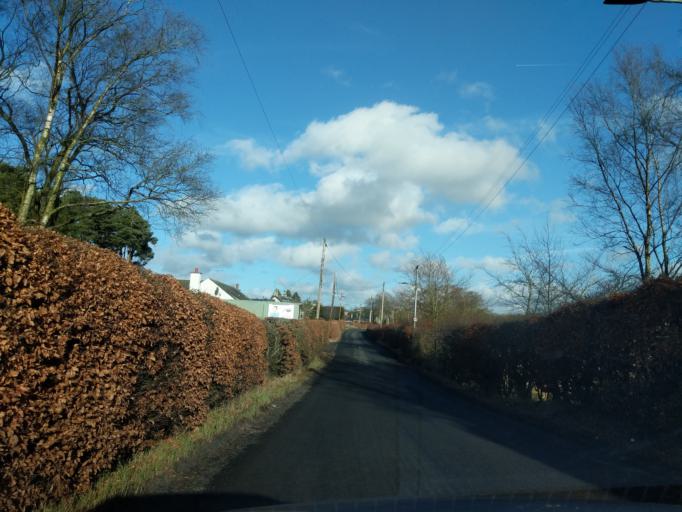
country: GB
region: Scotland
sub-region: South Lanarkshire
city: Carluke
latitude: 55.7214
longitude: -3.8376
